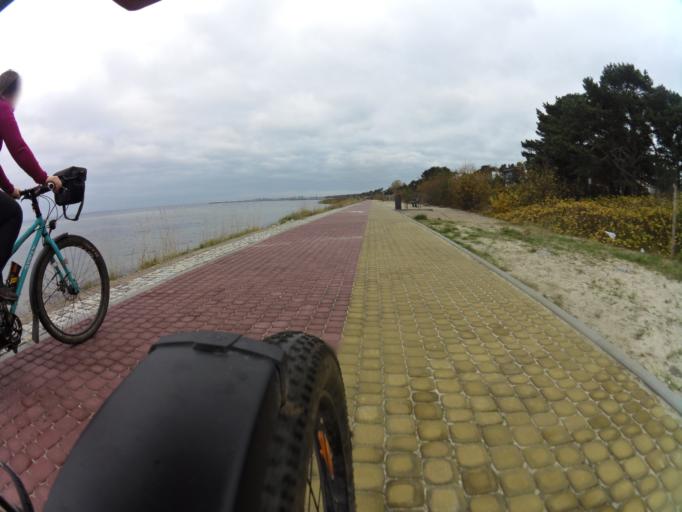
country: PL
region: Pomeranian Voivodeship
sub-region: Powiat pucki
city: Jastarnia
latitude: 54.6772
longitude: 18.7171
